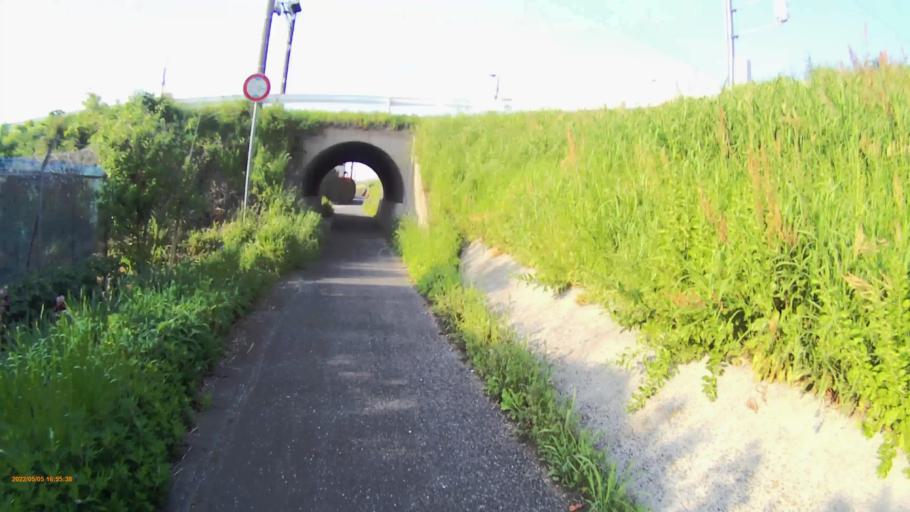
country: JP
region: Saitama
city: Kurihashi
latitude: 36.1089
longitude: 139.7238
